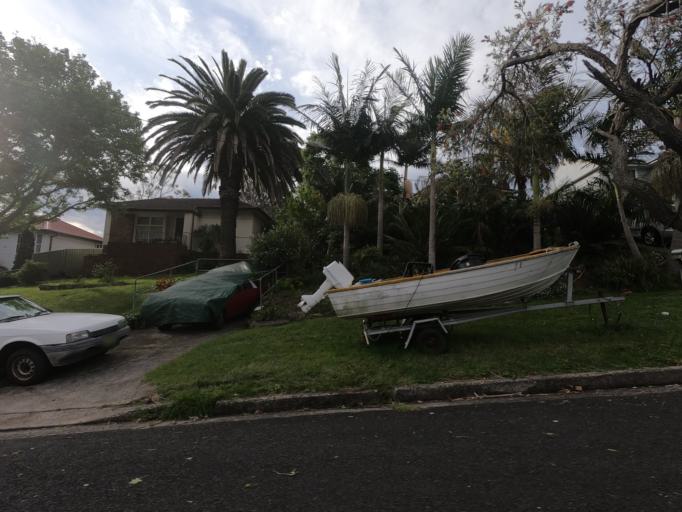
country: AU
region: New South Wales
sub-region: Wollongong
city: Berkeley
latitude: -34.4781
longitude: 150.8434
